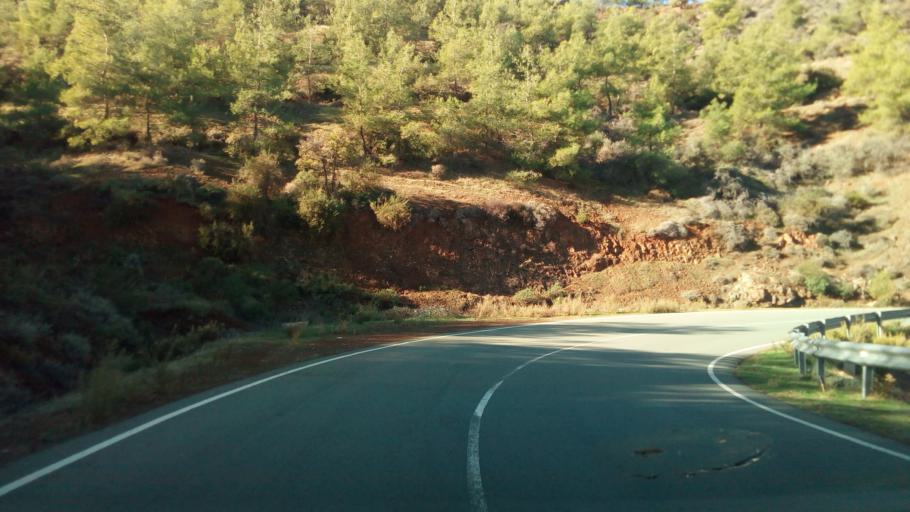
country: CY
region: Lefkosia
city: Kato Pyrgos
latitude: 35.1057
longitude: 32.7515
